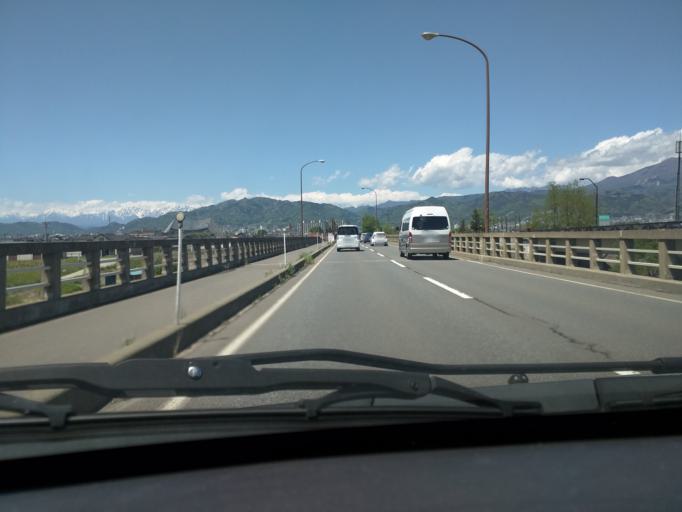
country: JP
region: Nagano
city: Suzaka
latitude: 36.6408
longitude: 138.2558
